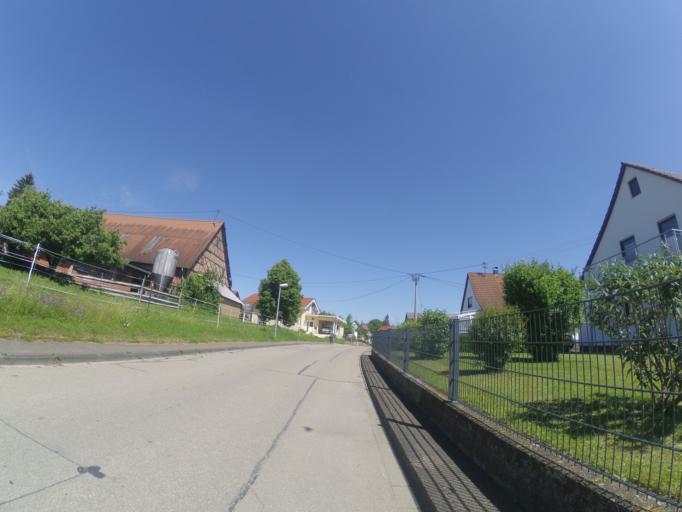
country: DE
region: Baden-Wuerttemberg
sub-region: Tuebingen Region
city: Dornstadt
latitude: 48.4810
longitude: 9.9119
